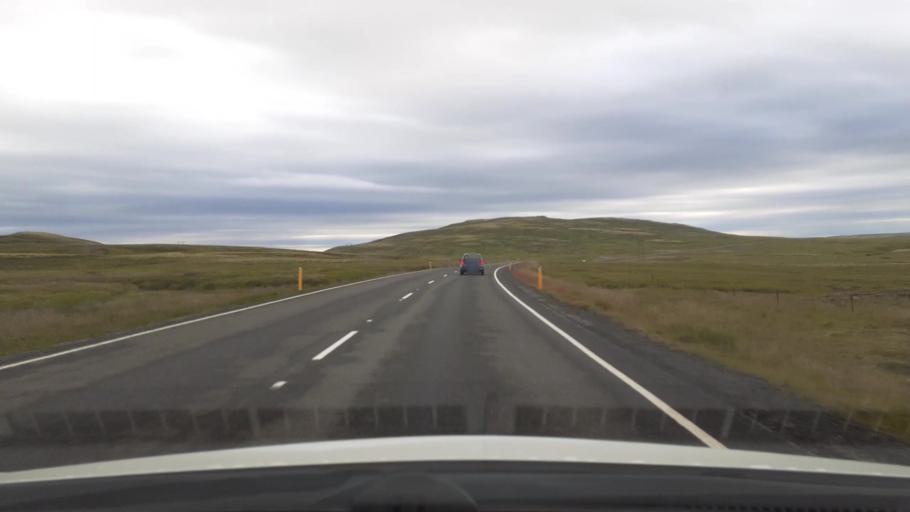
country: IS
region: Capital Region
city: Mosfellsbaer
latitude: 64.2087
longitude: -21.4377
